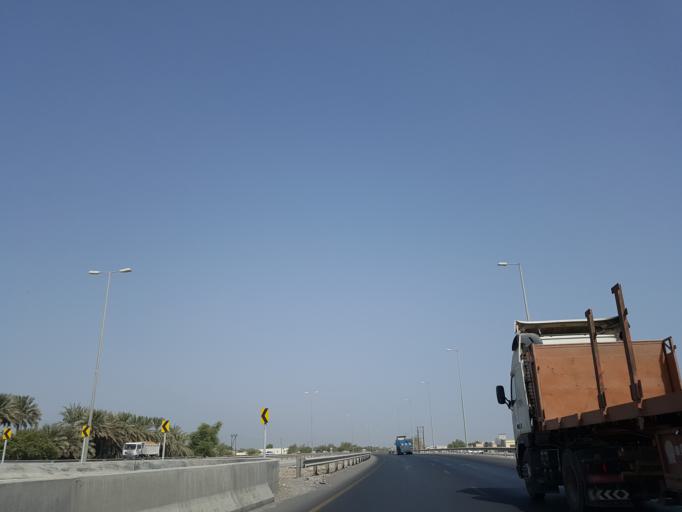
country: OM
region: Al Batinah
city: As Suwayq
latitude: 23.7639
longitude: 57.5515
